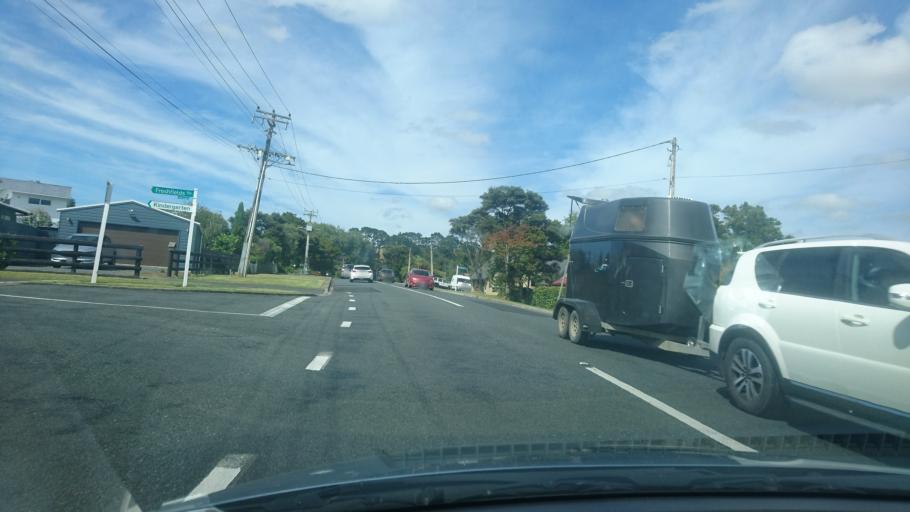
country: NZ
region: Auckland
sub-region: Auckland
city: Muriwai Beach
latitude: -36.7726
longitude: 174.4905
